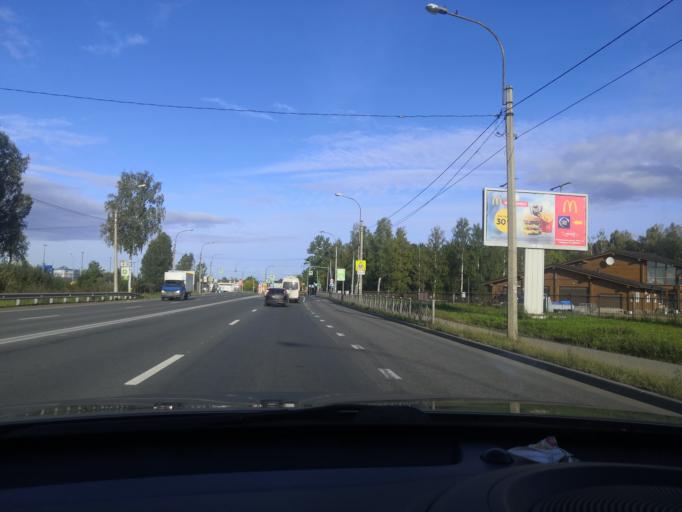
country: RU
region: St.-Petersburg
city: Pargolovo
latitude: 60.0750
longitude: 30.2771
